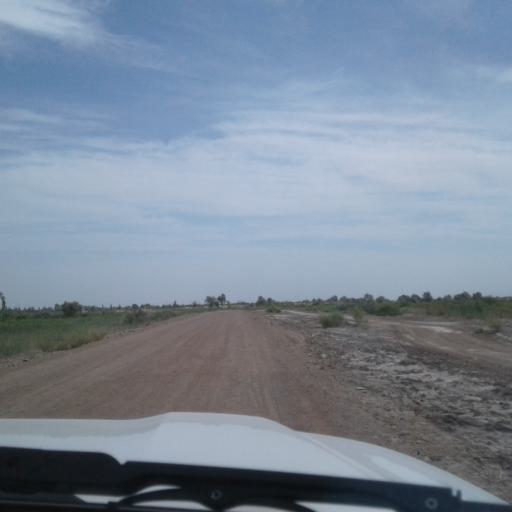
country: TM
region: Dasoguz
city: Tagta
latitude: 41.5510
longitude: 59.8131
